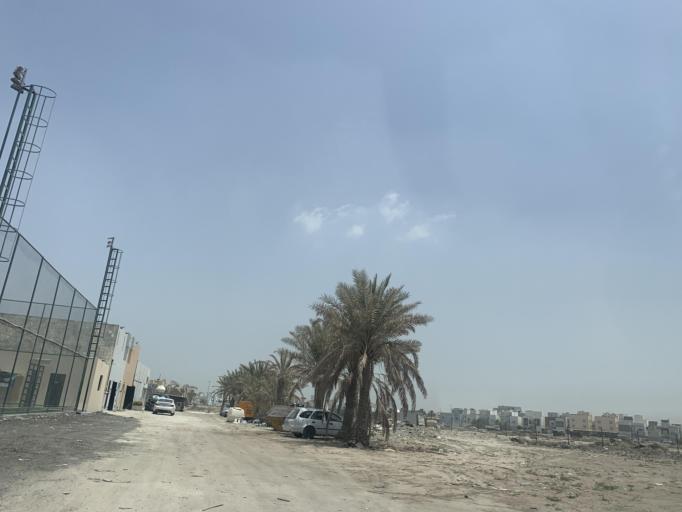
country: BH
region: Central Governorate
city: Madinat Hamad
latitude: 26.1527
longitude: 50.5036
